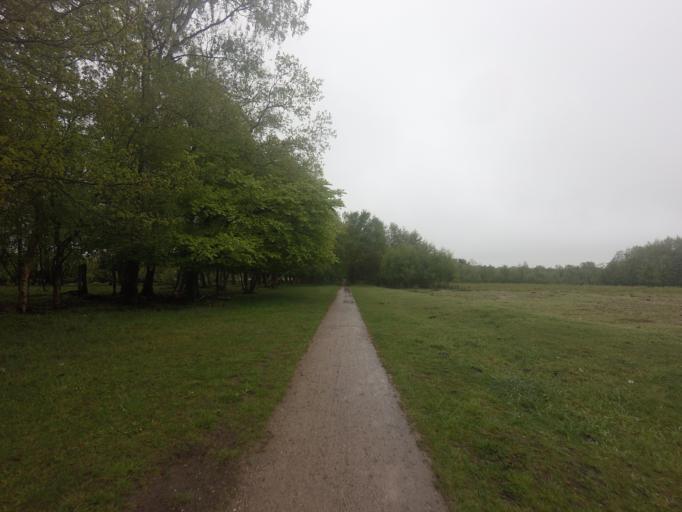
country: NL
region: Overijssel
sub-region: Gemeente Enschede
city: Enschede
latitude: 52.1447
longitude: 6.8666
